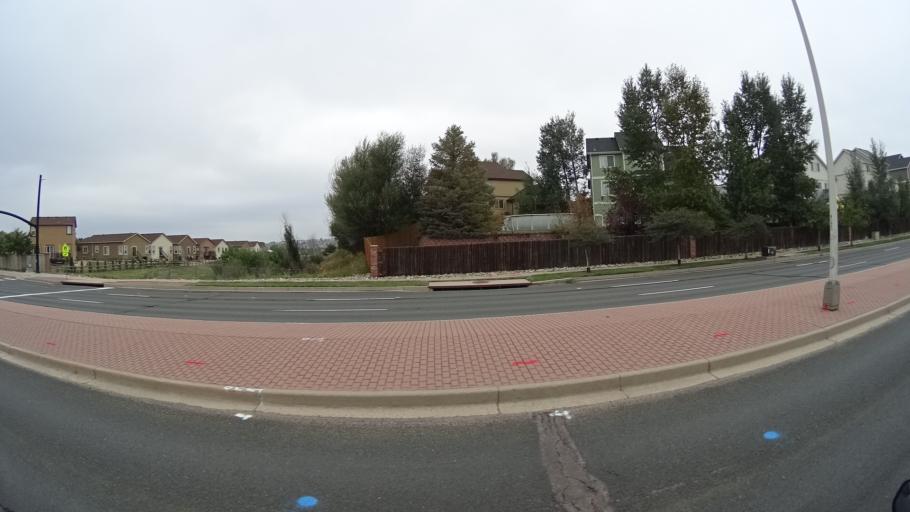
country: US
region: Colorado
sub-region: El Paso County
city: Cimarron Hills
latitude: 38.9061
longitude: -104.6964
